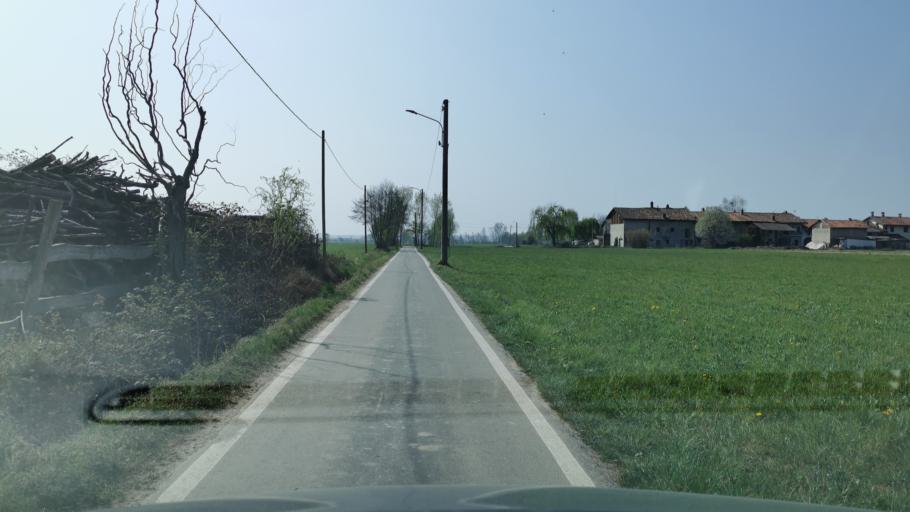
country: IT
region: Piedmont
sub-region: Provincia di Torino
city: Rivarolo Canavese
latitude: 45.3250
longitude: 7.7055
